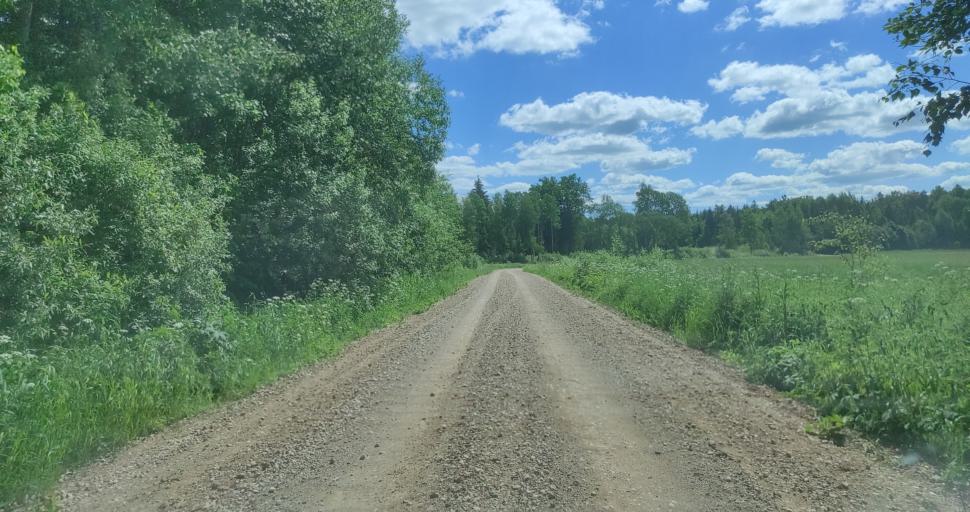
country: LV
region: Aizpute
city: Aizpute
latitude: 56.8433
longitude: 21.7112
